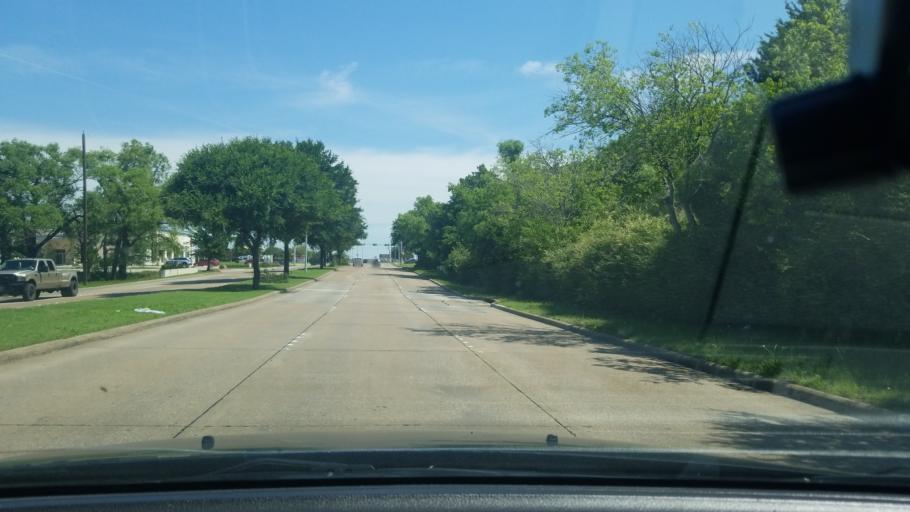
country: US
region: Texas
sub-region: Dallas County
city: Mesquite
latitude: 32.7864
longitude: -96.5957
